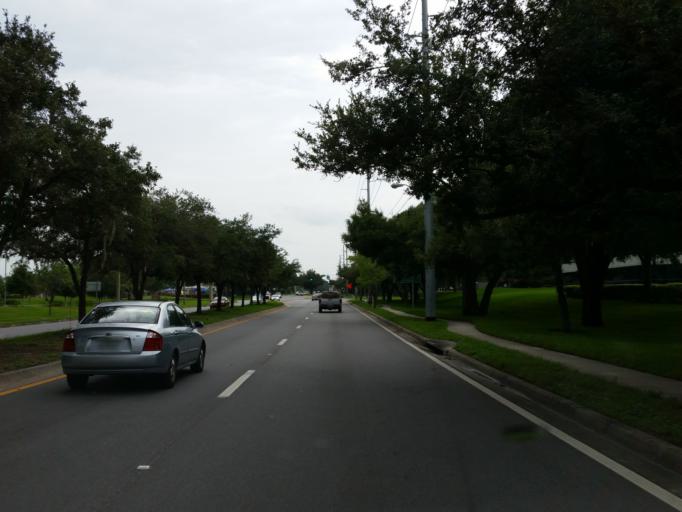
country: US
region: Florida
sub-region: Hillsborough County
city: Mango
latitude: 27.9776
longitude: -82.3352
